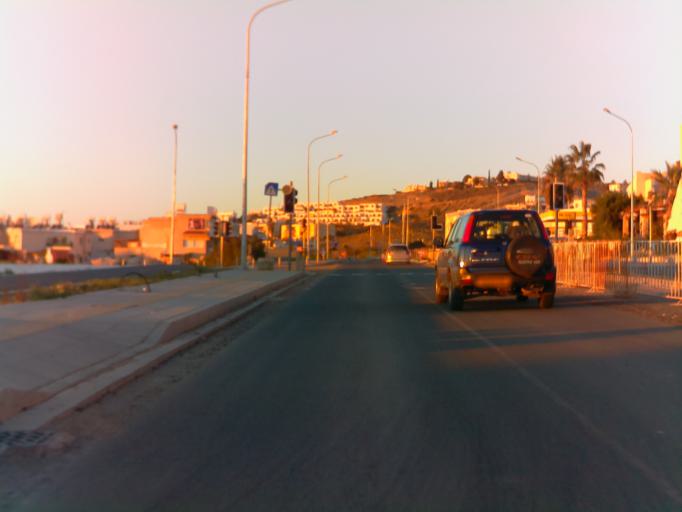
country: CY
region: Pafos
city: Chlorakas
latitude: 34.7826
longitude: 32.4058
